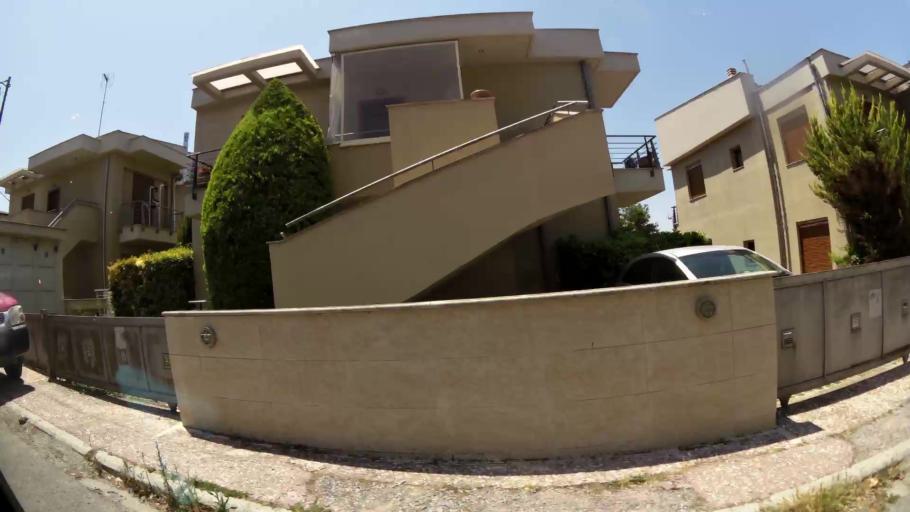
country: GR
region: Central Macedonia
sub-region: Nomos Thessalonikis
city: Plagiari
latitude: 40.4729
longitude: 22.9547
